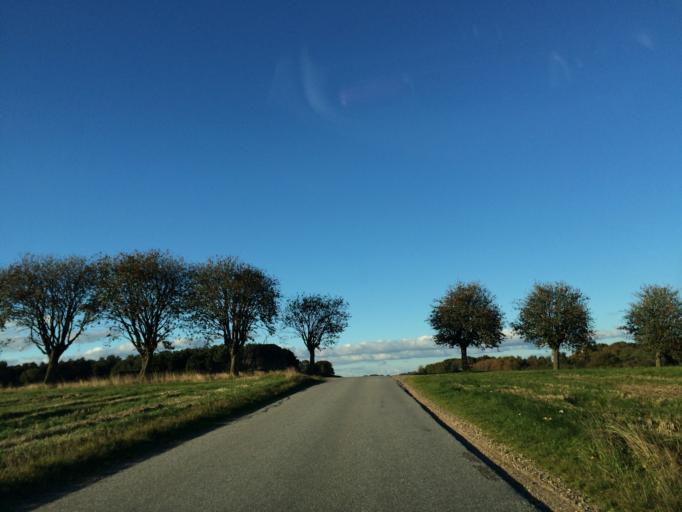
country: DK
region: Central Jutland
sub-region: Silkeborg Kommune
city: Svejbaek
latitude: 56.1740
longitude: 9.6936
